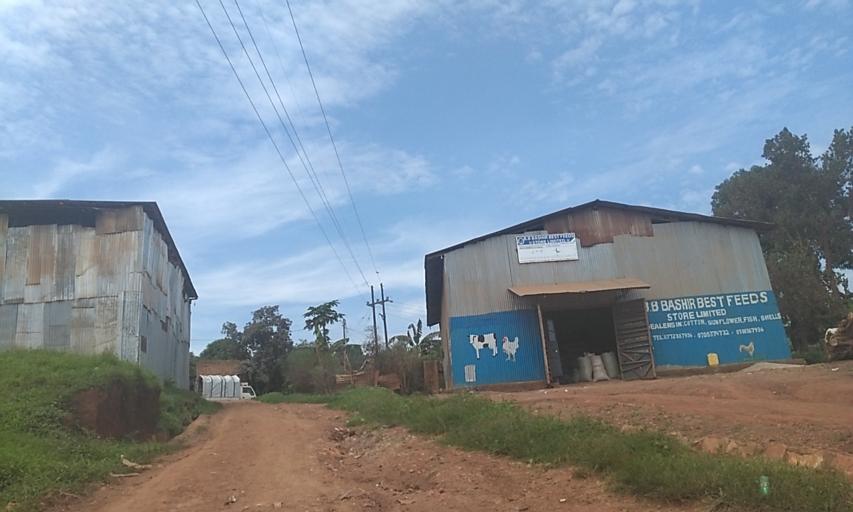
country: UG
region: Central Region
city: Kampala Central Division
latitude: 0.2933
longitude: 32.5200
